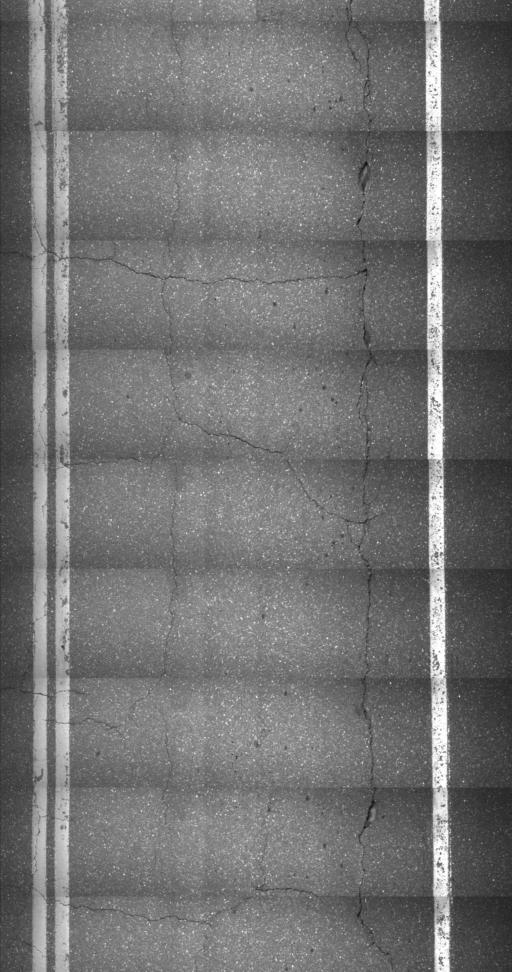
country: US
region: Vermont
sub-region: Caledonia County
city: Lyndonville
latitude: 44.5852
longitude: -72.0790
